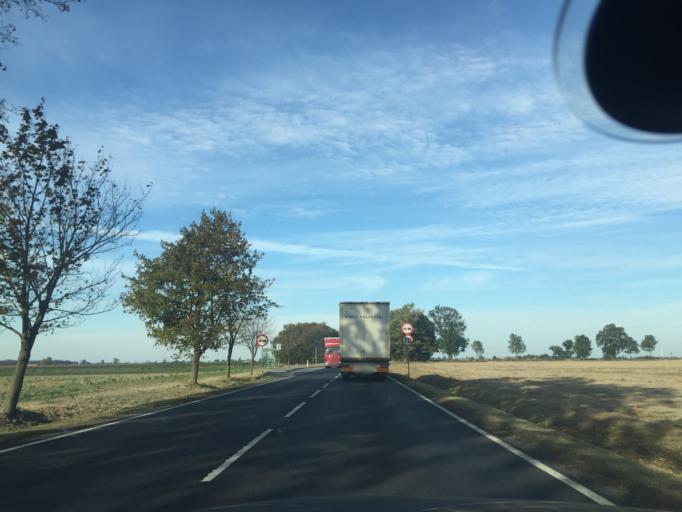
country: PL
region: Kujawsko-Pomorskie
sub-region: Powiat mogilenski
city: Strzelno
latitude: 52.6539
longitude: 18.1873
